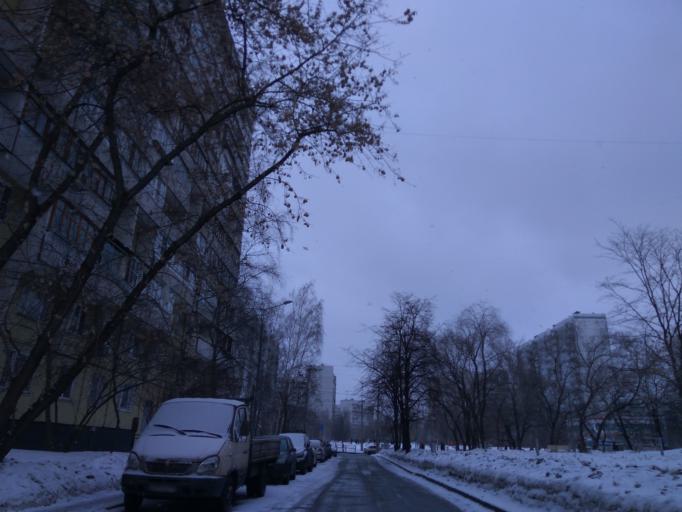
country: RU
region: Moscow
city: Strogino
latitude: 55.7983
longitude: 37.4020
